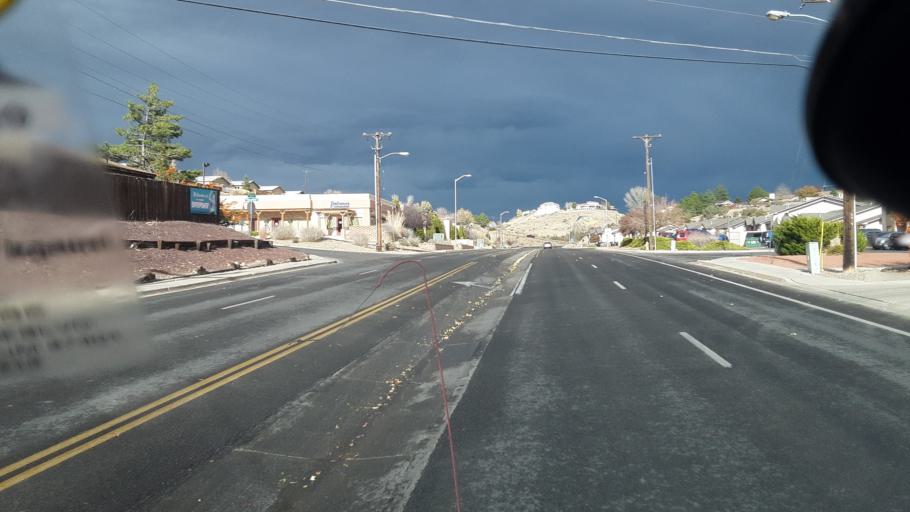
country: US
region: New Mexico
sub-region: San Juan County
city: Farmington
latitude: 36.7579
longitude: -108.1961
